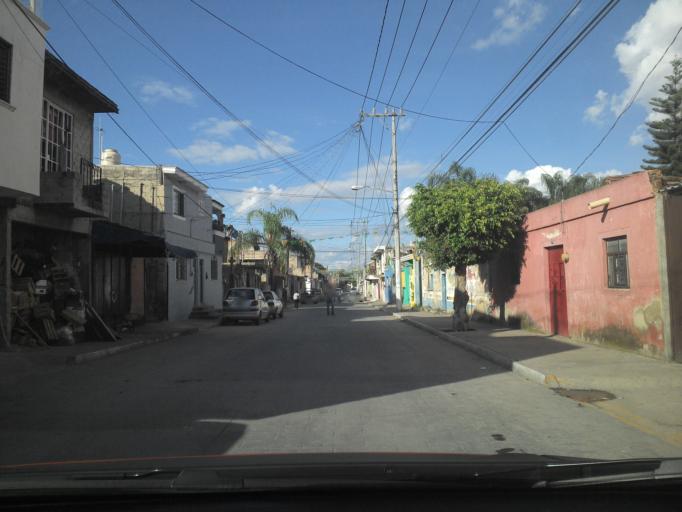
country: MX
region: Jalisco
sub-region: Tlajomulco de Zuniga
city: Palomar
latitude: 20.6201
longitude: -103.4544
